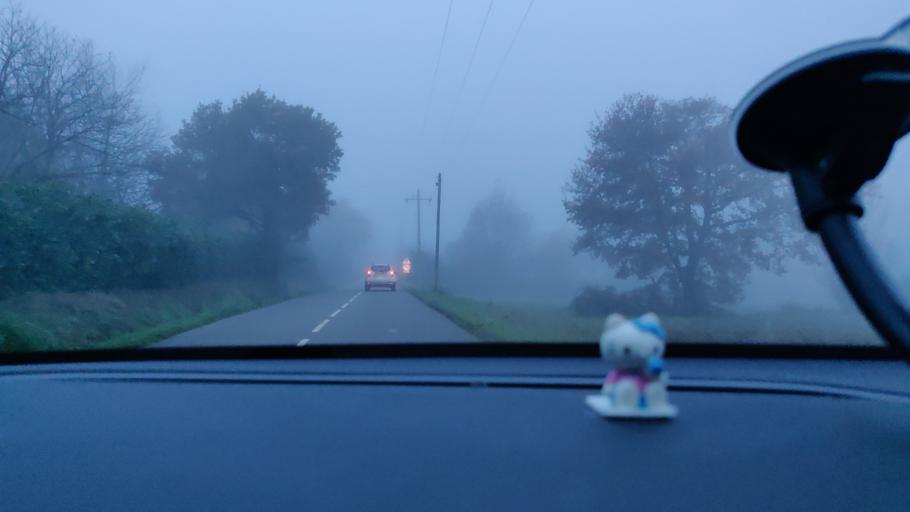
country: FR
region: Midi-Pyrenees
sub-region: Departement de la Haute-Garonne
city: Vieille-Toulouse
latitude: 43.4971
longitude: 1.4582
